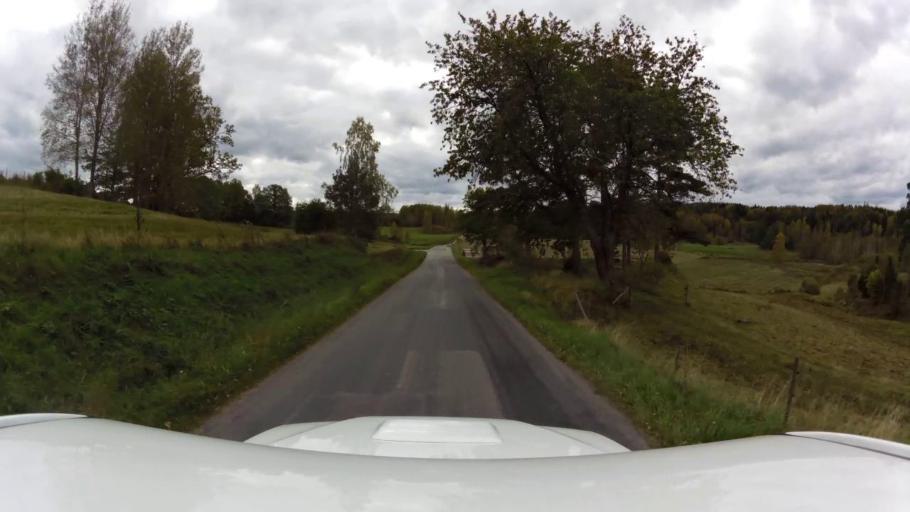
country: SE
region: OEstergoetland
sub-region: Kinda Kommun
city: Rimforsa
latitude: 58.1993
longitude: 15.5696
